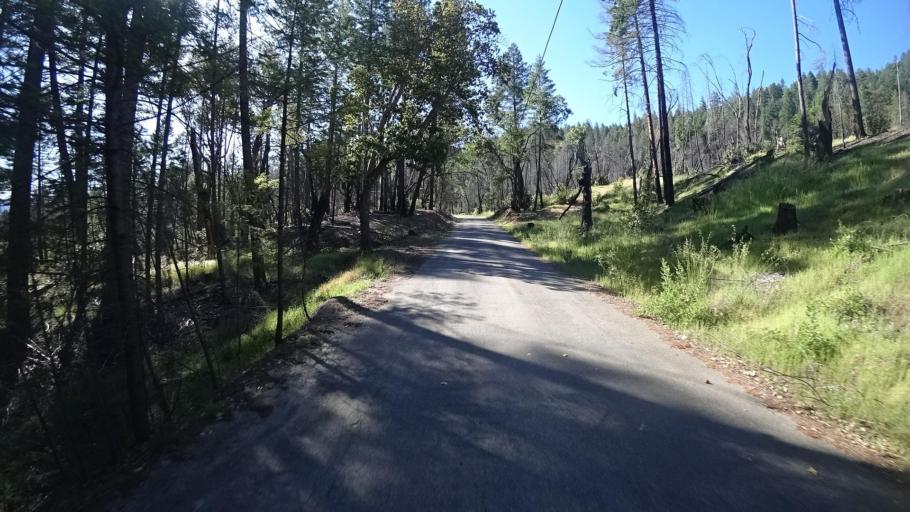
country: US
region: California
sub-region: Lake County
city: Upper Lake
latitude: 39.4036
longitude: -122.9680
